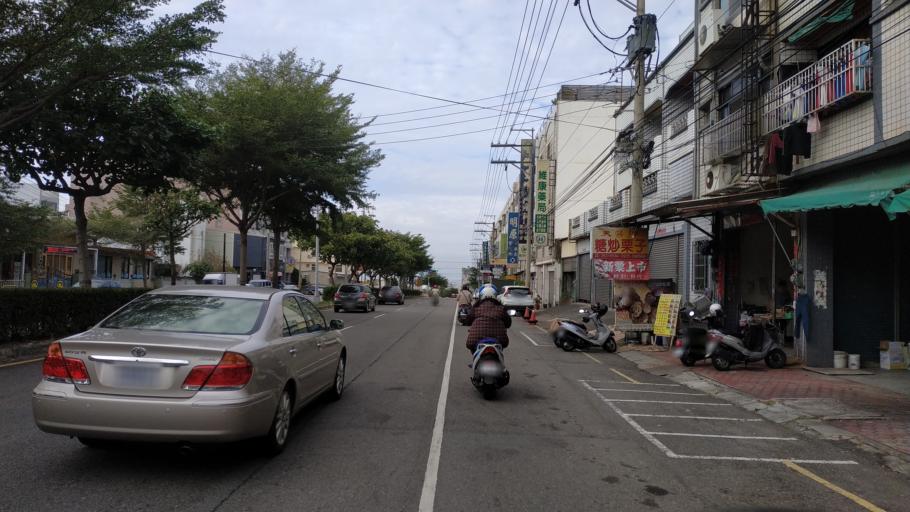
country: TW
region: Taiwan
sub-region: Taichung City
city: Taichung
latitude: 24.2299
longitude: 120.5667
